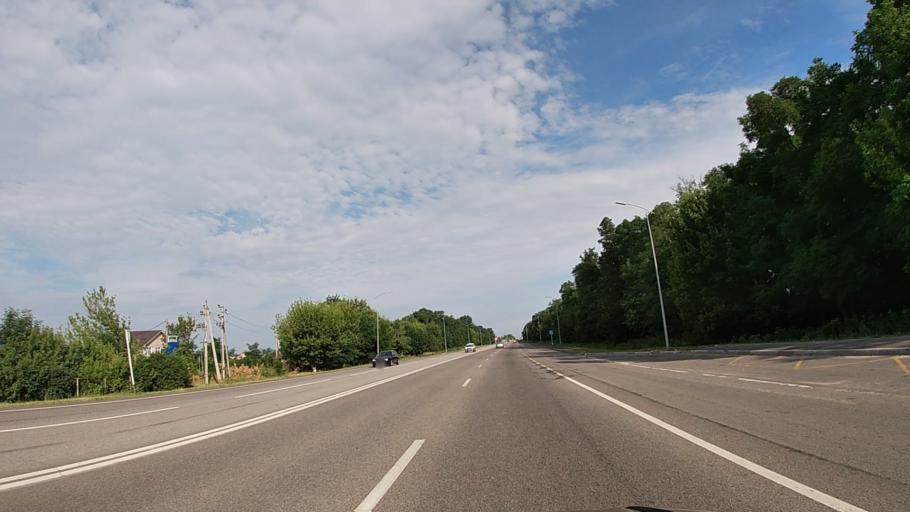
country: RU
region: Belgorod
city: Severnyy
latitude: 50.6388
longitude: 36.4422
